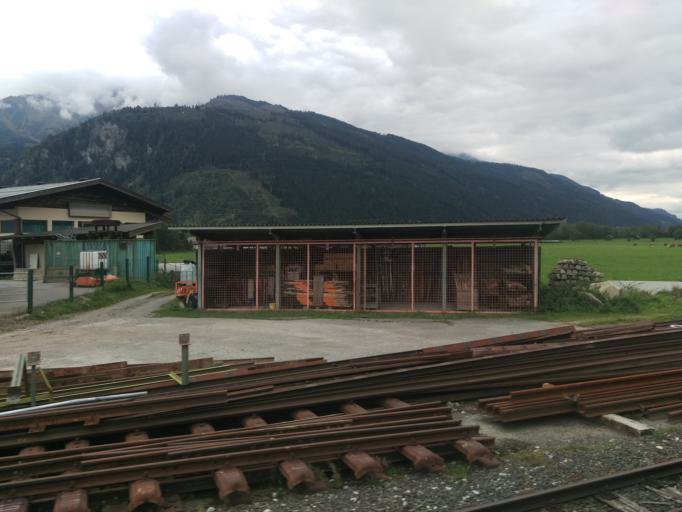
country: AT
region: Salzburg
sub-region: Politischer Bezirk Zell am See
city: Uttendorf
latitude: 47.2822
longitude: 12.5712
